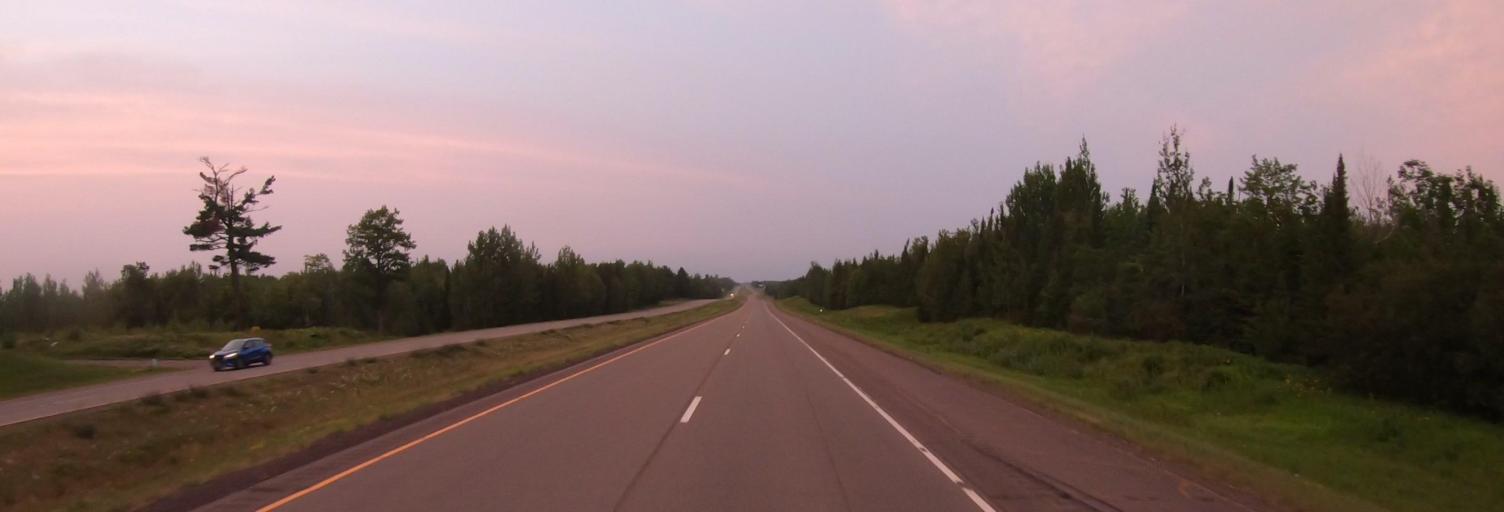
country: US
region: Minnesota
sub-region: Carlton County
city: Cloquet
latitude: 47.0154
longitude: -92.4709
